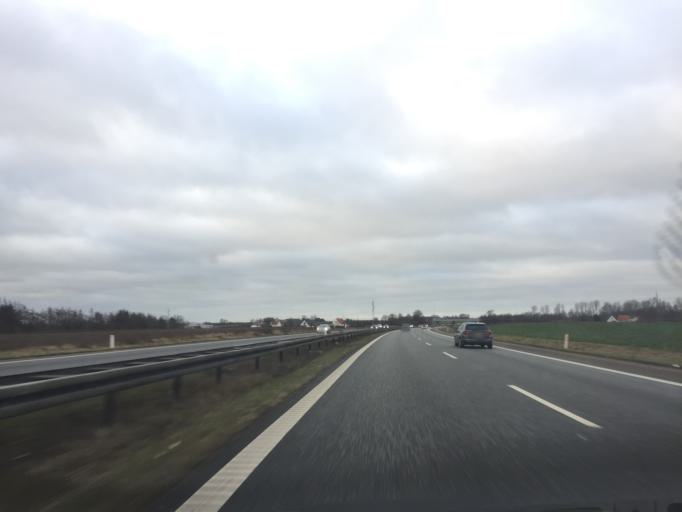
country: DK
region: Zealand
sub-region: Slagelse Kommune
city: Forlev
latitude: 55.3697
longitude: 11.2940
